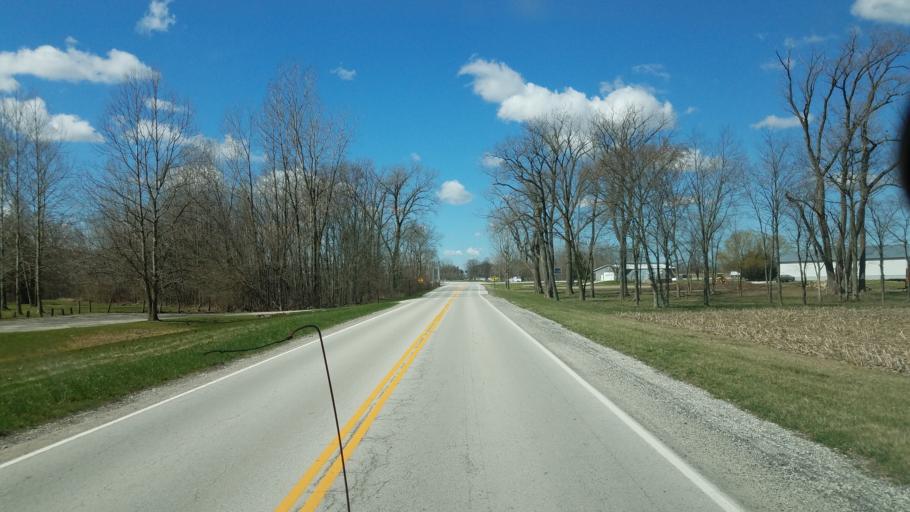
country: US
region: Ohio
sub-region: Sandusky County
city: Ballville
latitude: 41.2916
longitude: -83.1666
